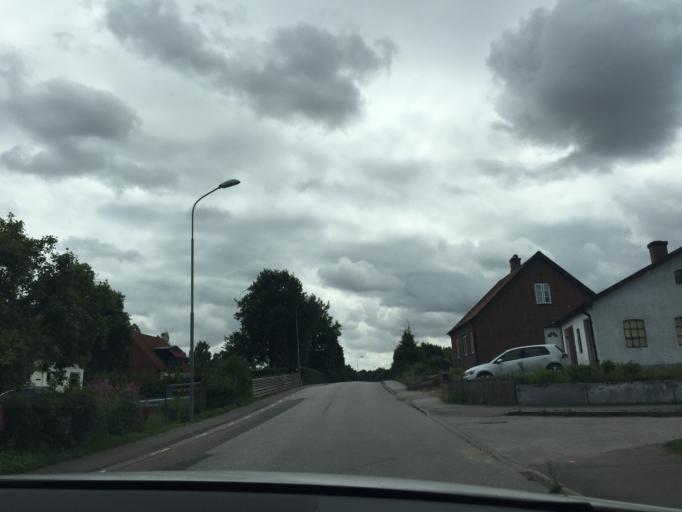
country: SE
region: Skane
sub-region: Sjobo Kommun
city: Blentarp
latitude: 55.5888
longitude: 13.5998
